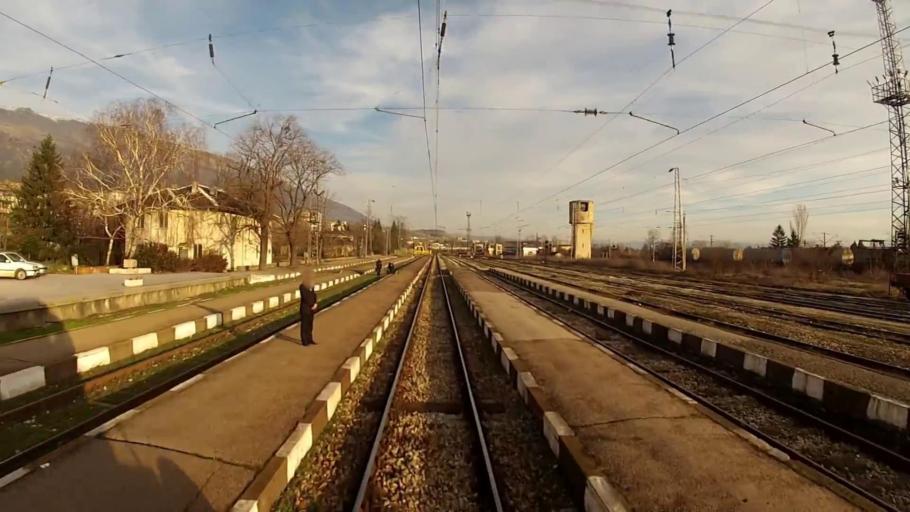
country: BG
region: Plovdiv
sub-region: Obshtina Karlovo
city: Karlovo
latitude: 42.6316
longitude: 24.8011
